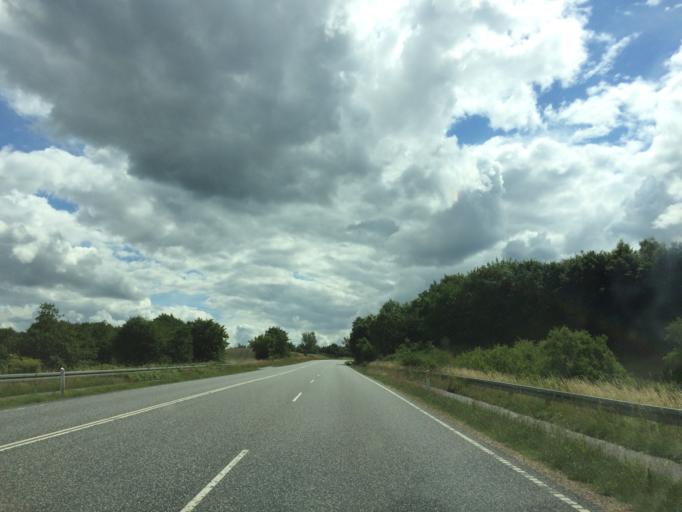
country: DK
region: North Denmark
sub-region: Vesthimmerland Kommune
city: Alestrup
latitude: 56.5624
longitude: 9.4830
